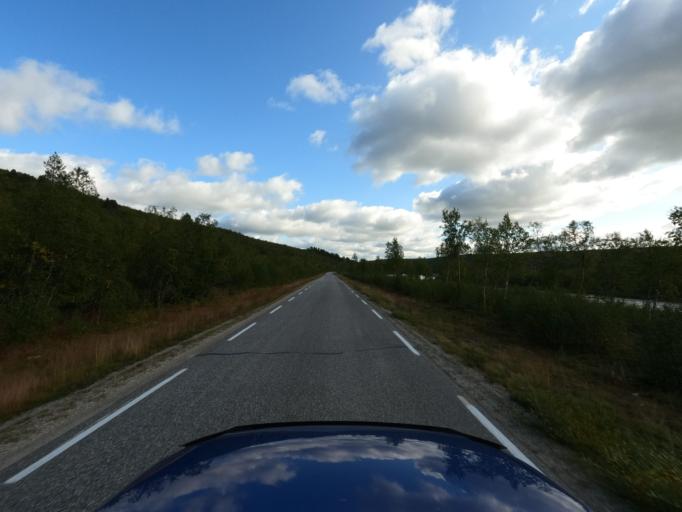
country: NO
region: Finnmark Fylke
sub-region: Porsanger
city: Lakselv
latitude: 69.4238
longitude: 24.8322
